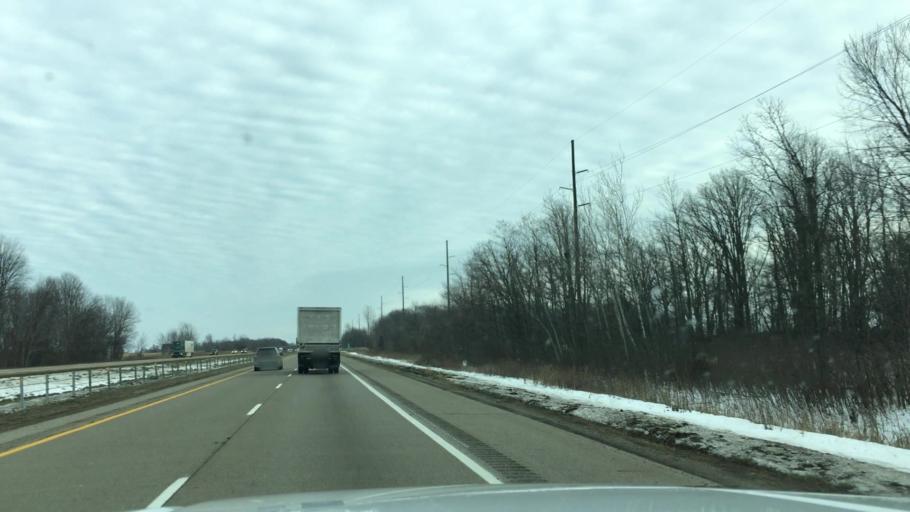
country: US
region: Michigan
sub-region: Ionia County
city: Portland
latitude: 42.8790
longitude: -85.0066
